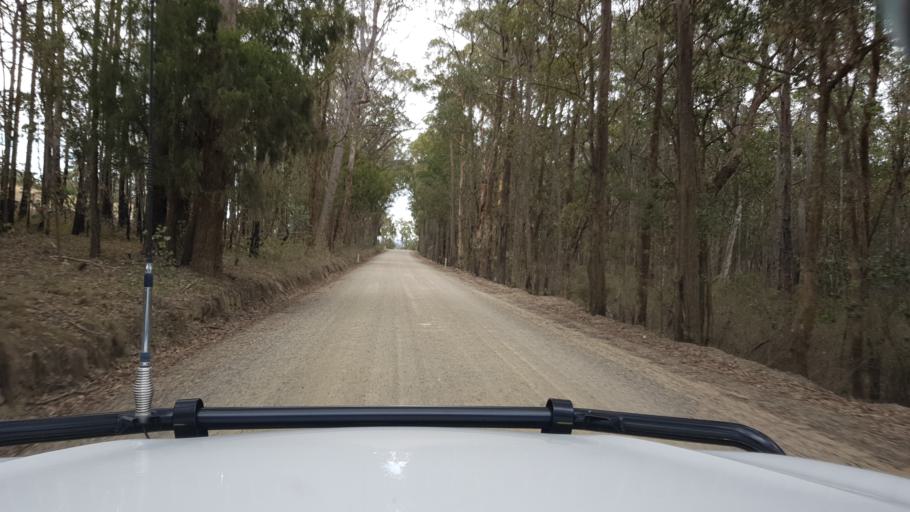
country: AU
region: Victoria
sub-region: East Gippsland
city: Bairnsdale
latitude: -37.6867
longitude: 147.5604
